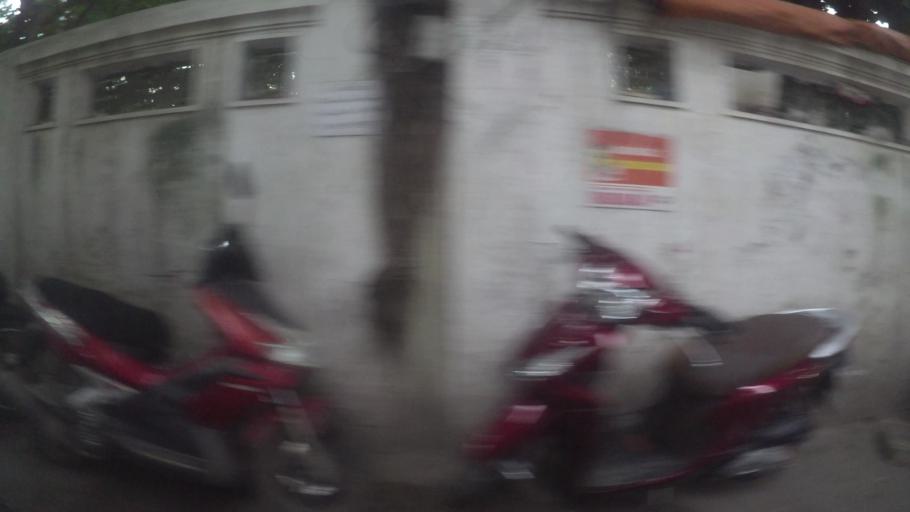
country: VN
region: Ha Noi
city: Cau Dien
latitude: 21.0303
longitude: 105.7711
